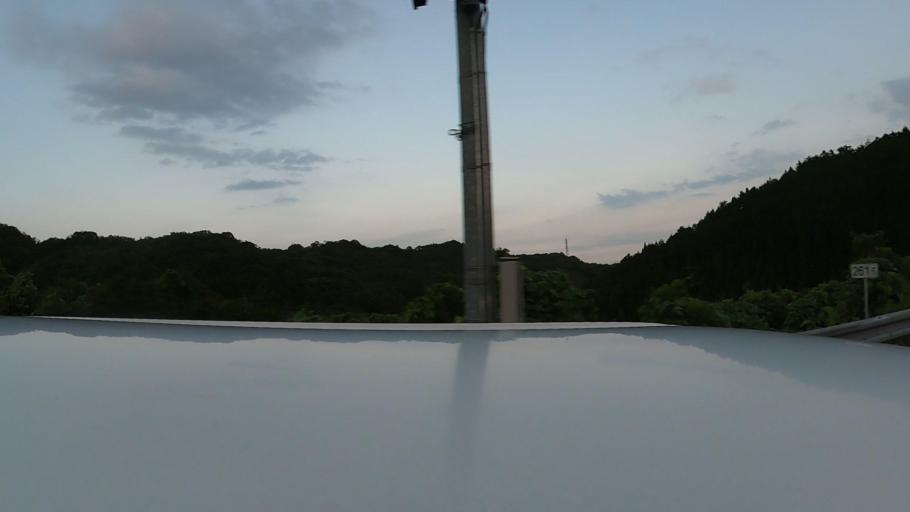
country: JP
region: Miyazaki
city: Nobeoka
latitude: 32.4551
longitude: 131.6129
